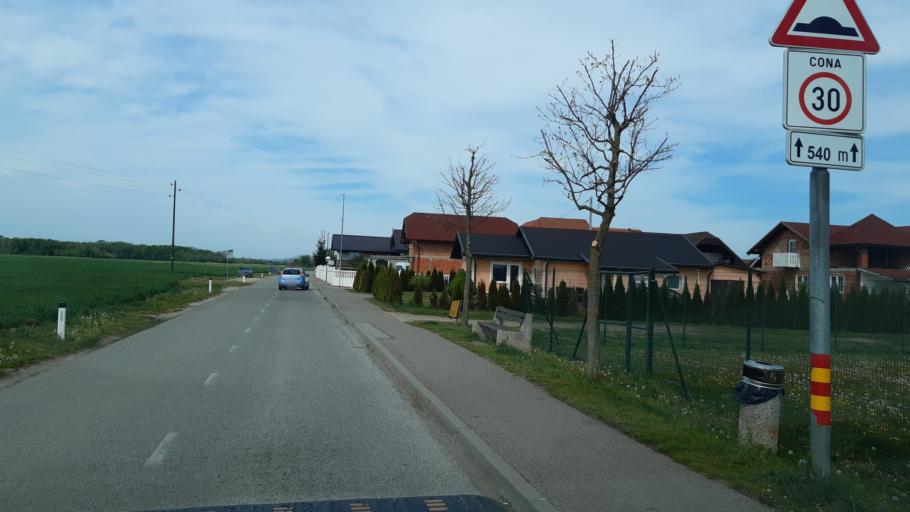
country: SI
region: Murska Sobota
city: Cernelavci
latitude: 46.6535
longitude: 16.1399
